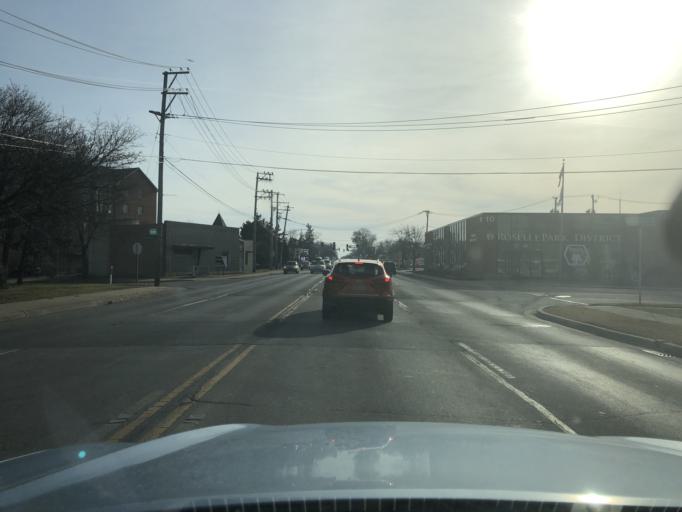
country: US
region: Illinois
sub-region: DuPage County
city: Roselle
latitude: 41.9865
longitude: -88.0803
